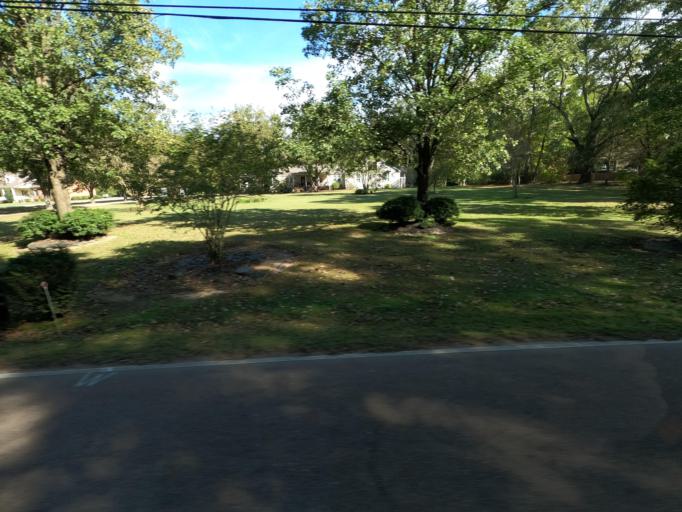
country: US
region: Tennessee
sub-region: Fayette County
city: Hickory Withe
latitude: 35.2143
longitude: -89.6504
